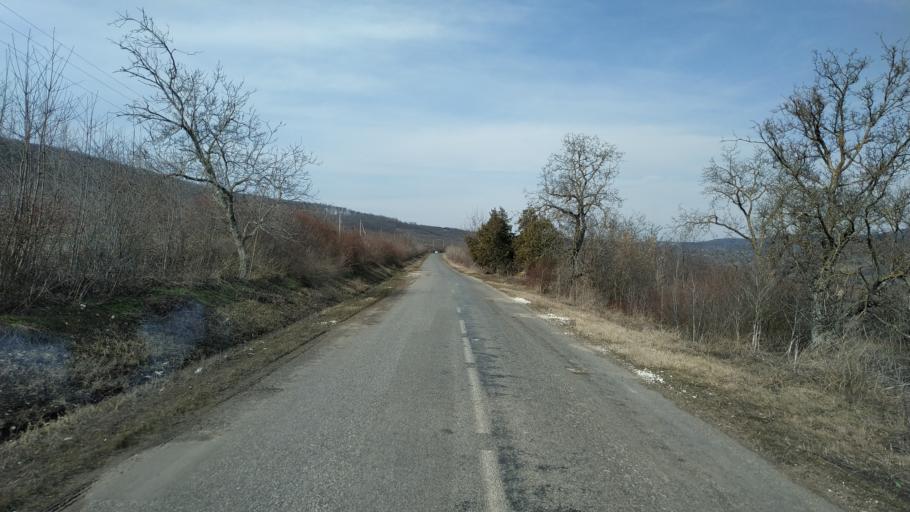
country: MD
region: Nisporeni
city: Nisporeni
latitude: 47.1771
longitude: 28.0843
